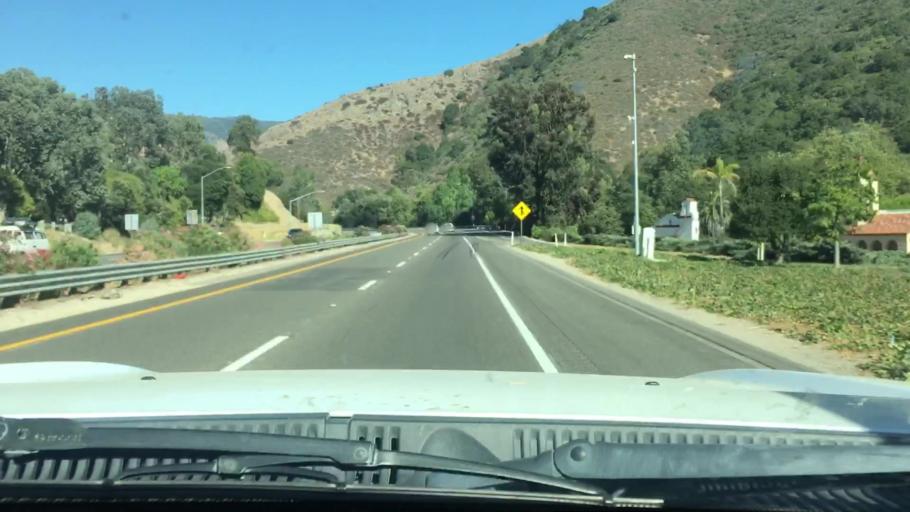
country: US
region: California
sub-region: San Luis Obispo County
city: San Luis Obispo
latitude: 35.2916
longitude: -120.6555
